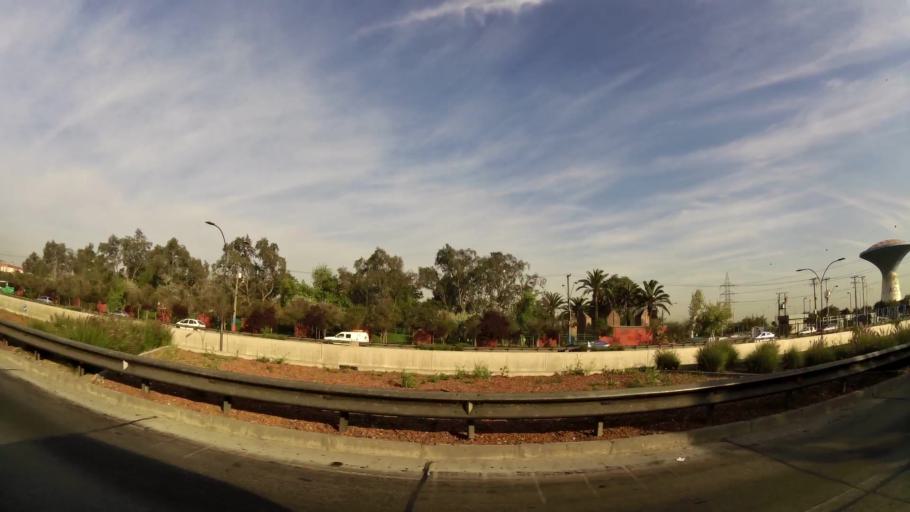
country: CL
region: Santiago Metropolitan
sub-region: Provincia de Santiago
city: Santiago
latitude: -33.5222
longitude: -70.6763
